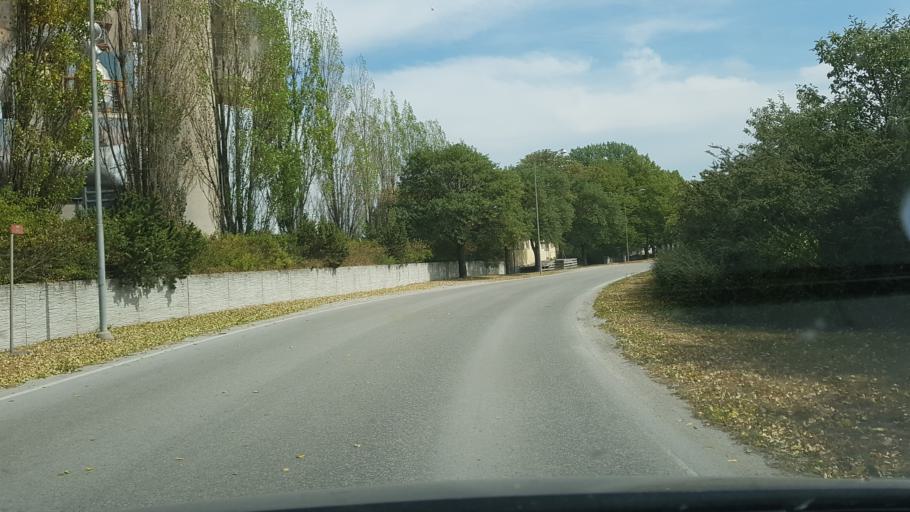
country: SE
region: Gotland
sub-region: Gotland
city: Slite
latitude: 57.7089
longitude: 18.7997
